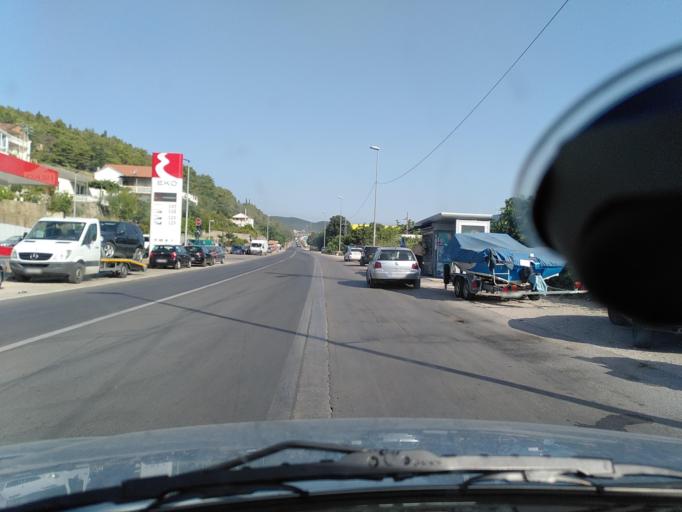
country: ME
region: Ulcinj
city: Ulcinj
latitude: 41.9371
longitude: 19.2191
